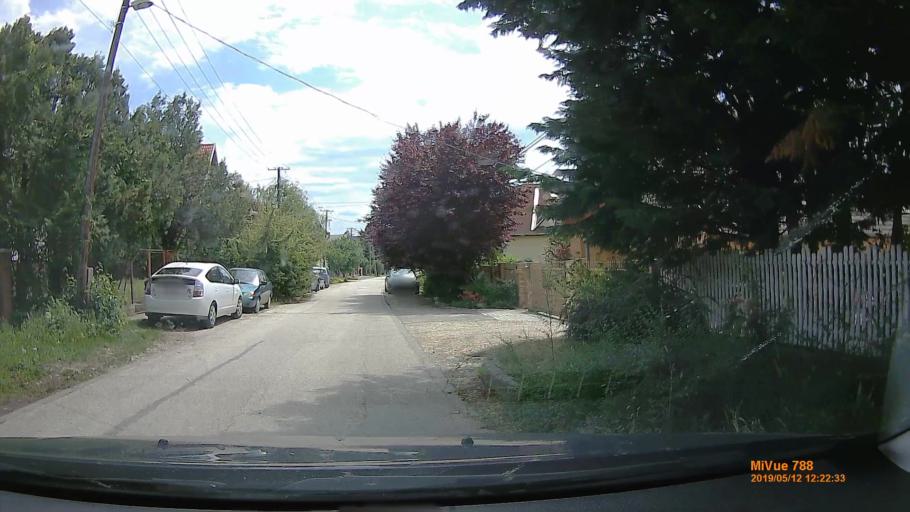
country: HU
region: Pest
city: Ecser
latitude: 47.4606
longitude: 19.2927
